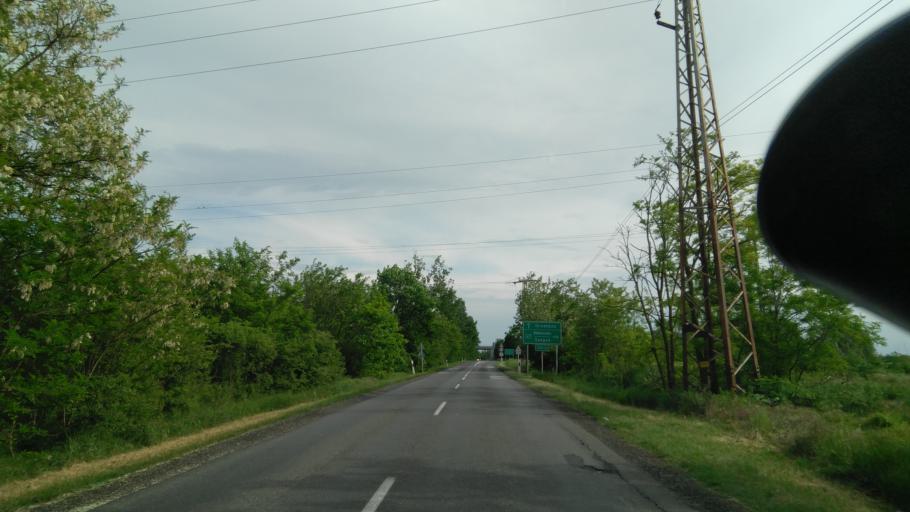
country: HU
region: Bekes
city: Oroshaza
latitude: 46.5988
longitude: 20.6821
